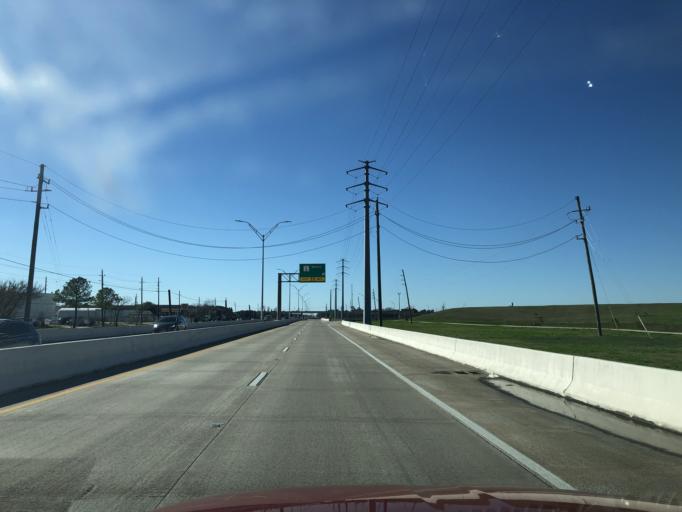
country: US
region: Texas
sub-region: Fort Bend County
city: Mission Bend
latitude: 29.7115
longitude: -95.6357
